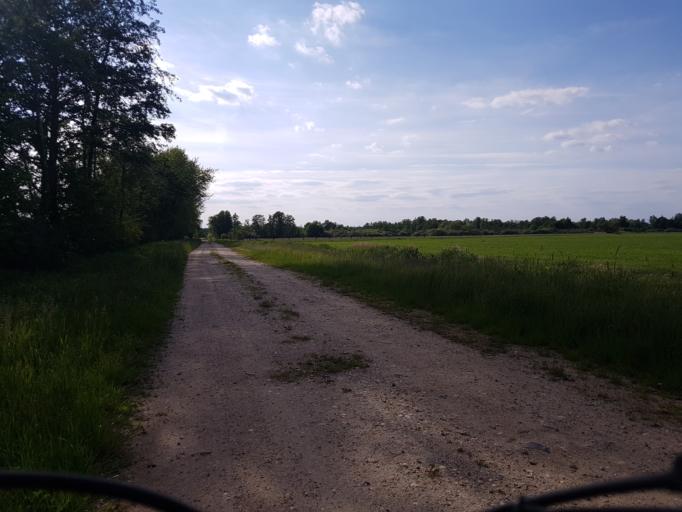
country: DE
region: Brandenburg
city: Groden
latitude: 51.4160
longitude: 13.5617
